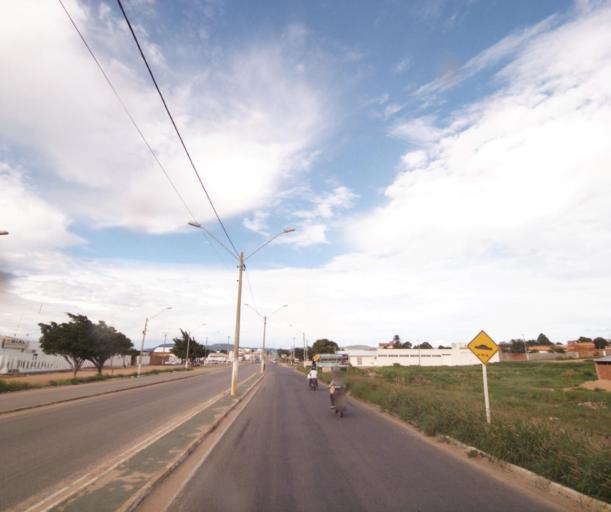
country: BR
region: Bahia
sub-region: Guanambi
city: Guanambi
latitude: -14.2074
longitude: -42.7629
